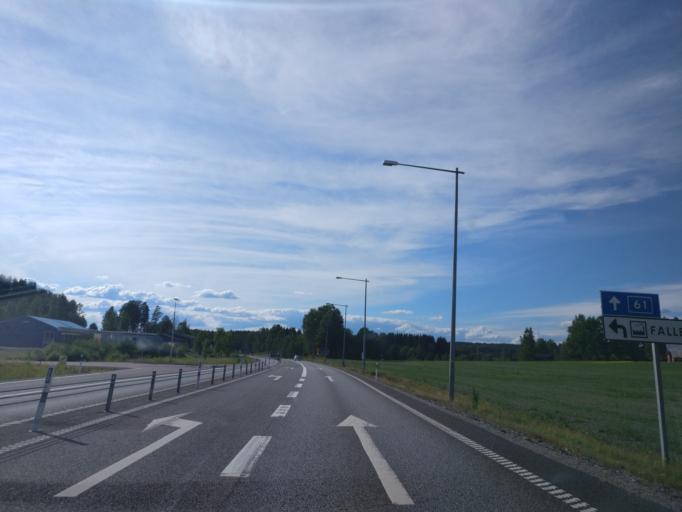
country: SE
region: Vaermland
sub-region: Arvika Kommun
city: Arvika
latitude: 59.6594
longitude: 12.6404
